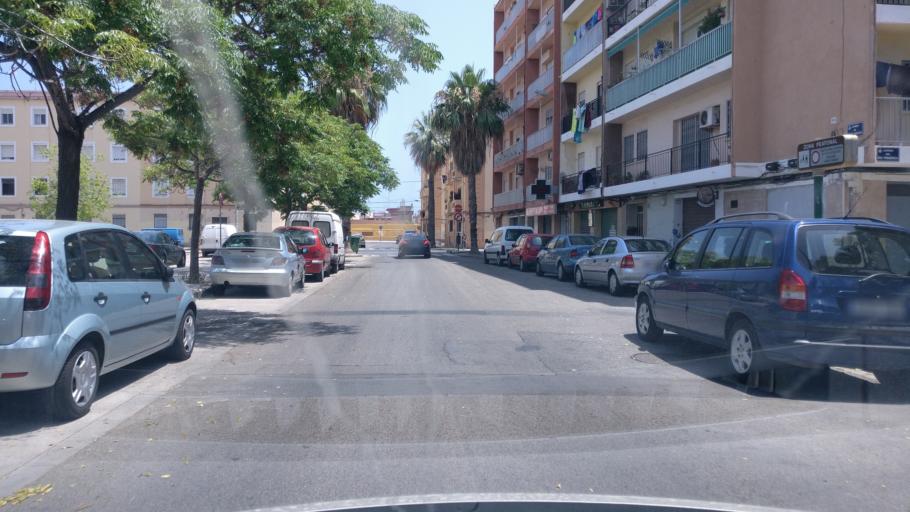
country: ES
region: Valencia
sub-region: Provincia de Valencia
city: Alboraya
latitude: 39.4790
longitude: -0.3306
